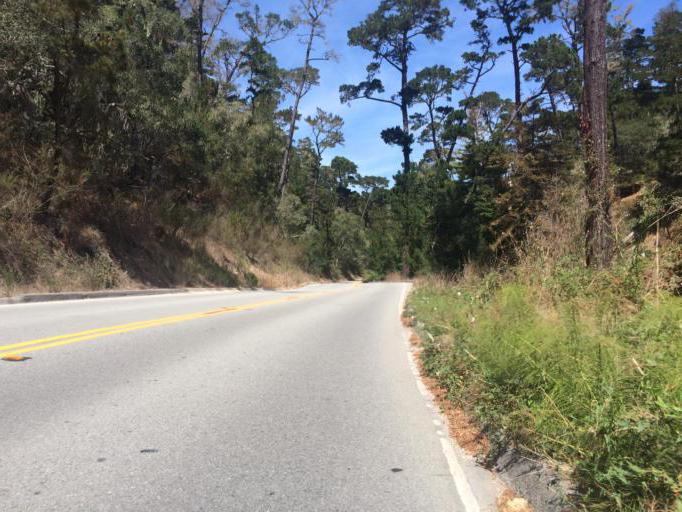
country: US
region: California
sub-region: Monterey County
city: Carmel-by-the-Sea
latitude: 36.5636
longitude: -121.9253
